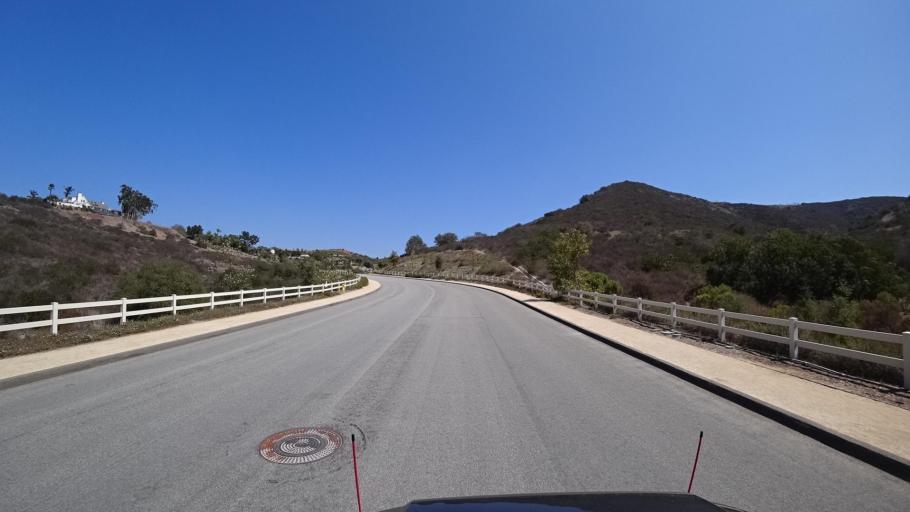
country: US
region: California
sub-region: San Diego County
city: San Marcos
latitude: 33.1849
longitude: -117.1926
